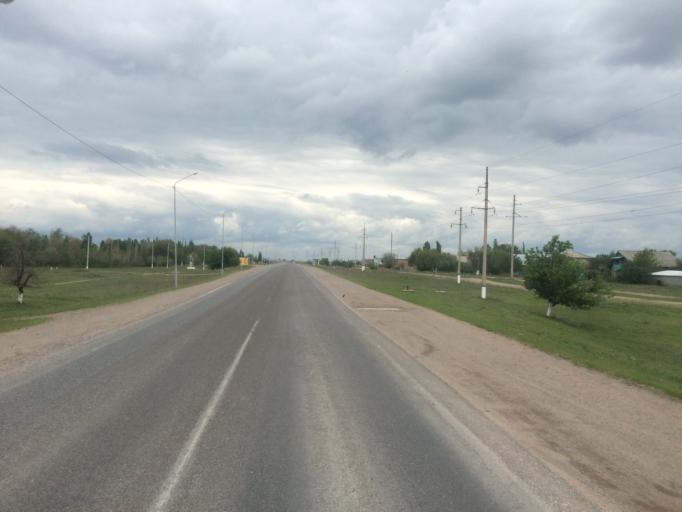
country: KG
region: Chuy
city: Sokuluk
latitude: 43.2498
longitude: 74.2901
